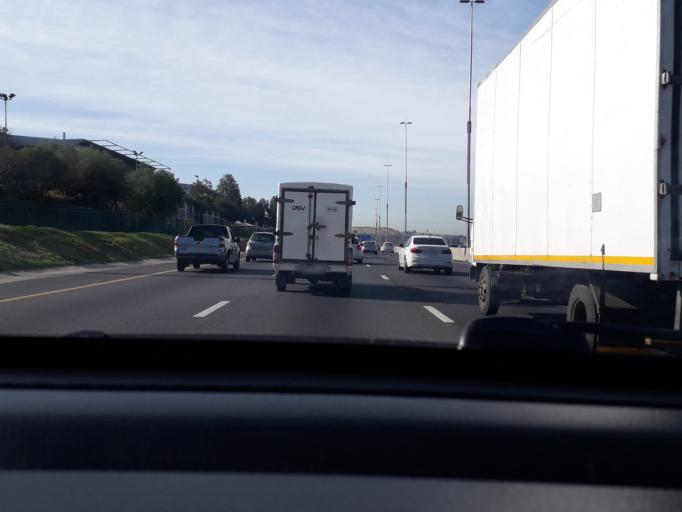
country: ZA
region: Gauteng
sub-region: City of Johannesburg Metropolitan Municipality
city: Modderfontein
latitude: -26.0679
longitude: 28.1105
